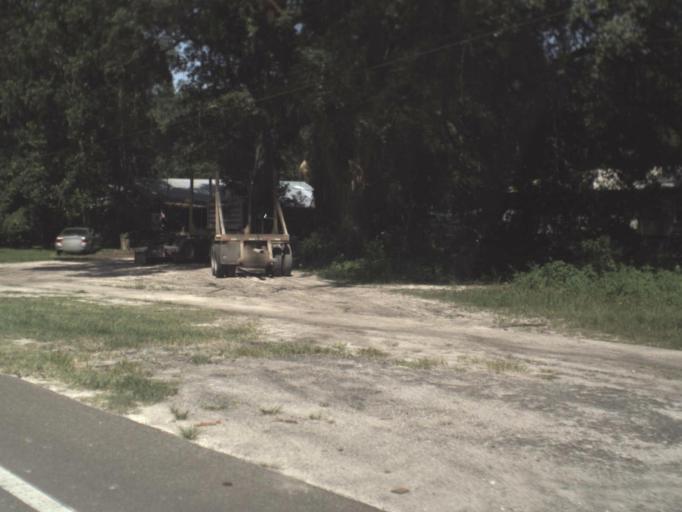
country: US
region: Florida
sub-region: Gilchrist County
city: Trenton
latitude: 29.6228
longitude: -82.8133
